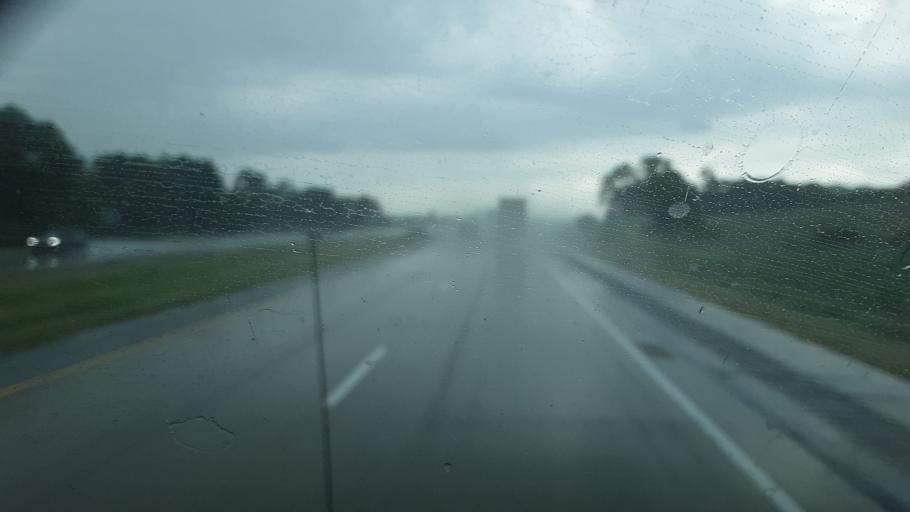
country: US
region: Iowa
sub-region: Pottawattamie County
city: Council Bluffs
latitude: 41.2984
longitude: -95.7728
